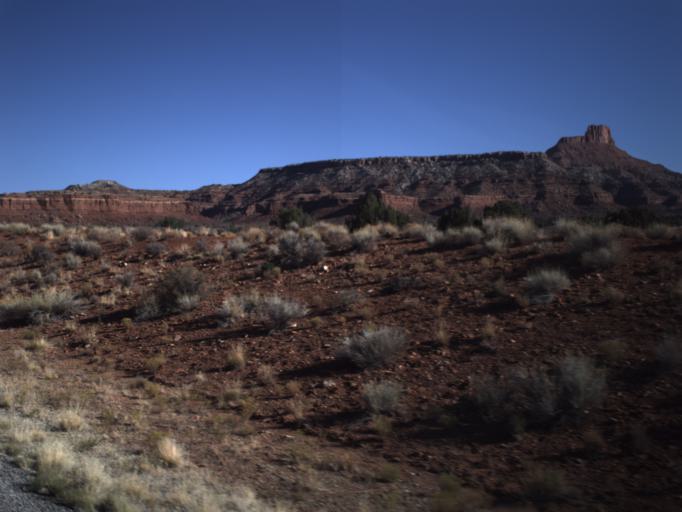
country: US
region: Utah
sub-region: San Juan County
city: Blanding
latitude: 37.6974
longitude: -110.2311
